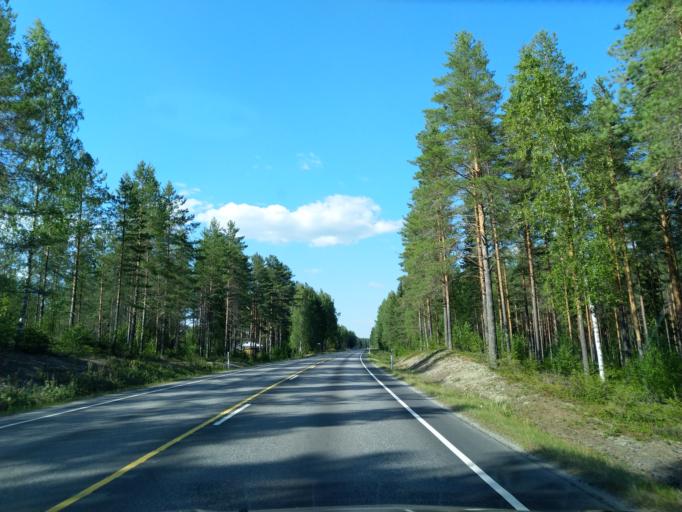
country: FI
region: Pirkanmaa
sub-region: Luoteis-Pirkanmaa
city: Kihnioe
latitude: 62.1131
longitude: 23.1023
